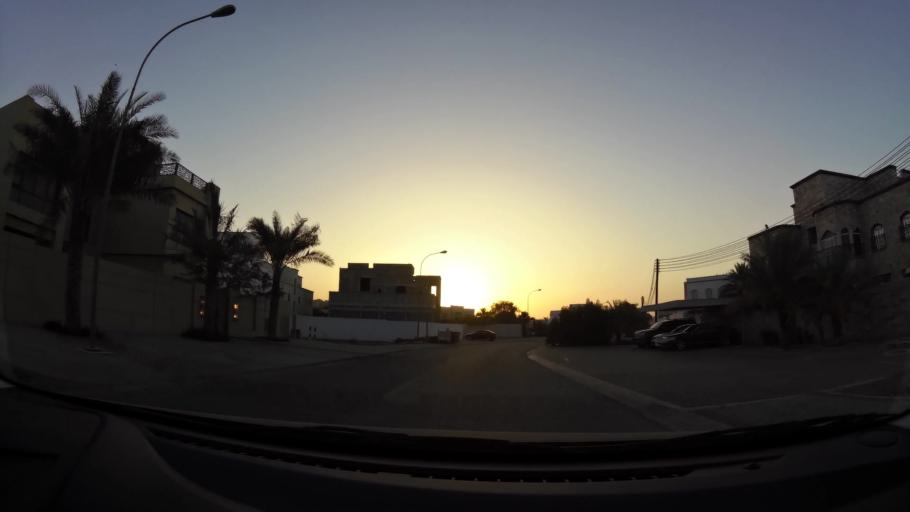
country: OM
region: Muhafazat Masqat
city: As Sib al Jadidah
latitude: 23.6428
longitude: 58.2091
